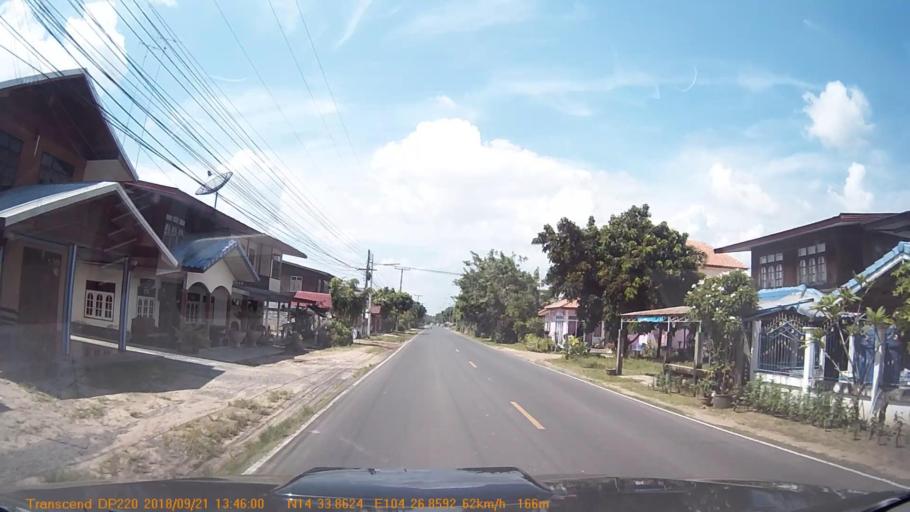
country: TH
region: Sisaket
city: Khun Han
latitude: 14.5648
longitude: 104.4476
